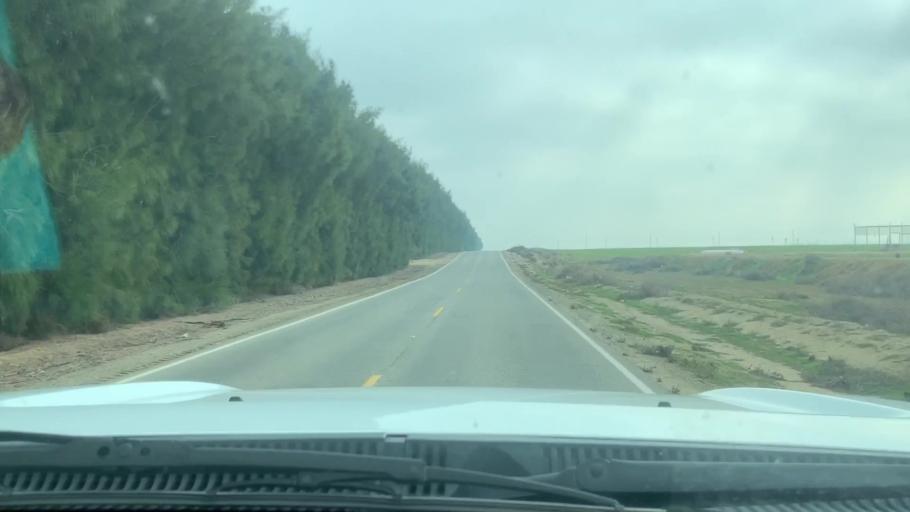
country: US
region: California
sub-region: Kern County
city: Lost Hills
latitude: 35.5069
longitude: -119.7453
